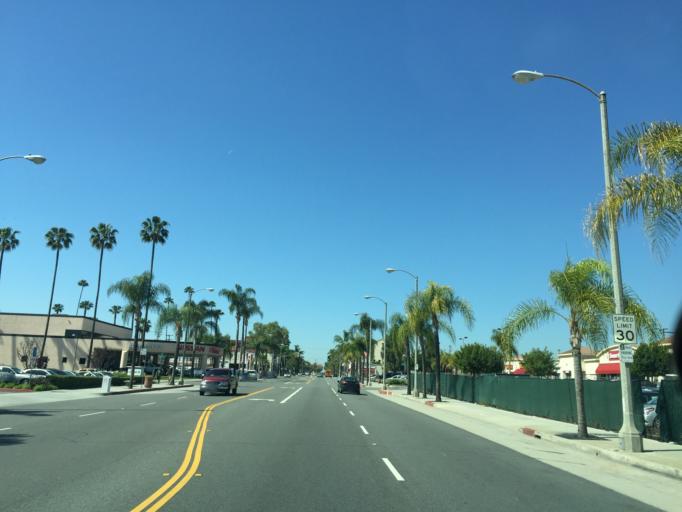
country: US
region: California
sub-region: Los Angeles County
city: Alhambra
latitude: 34.0994
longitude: -118.1180
